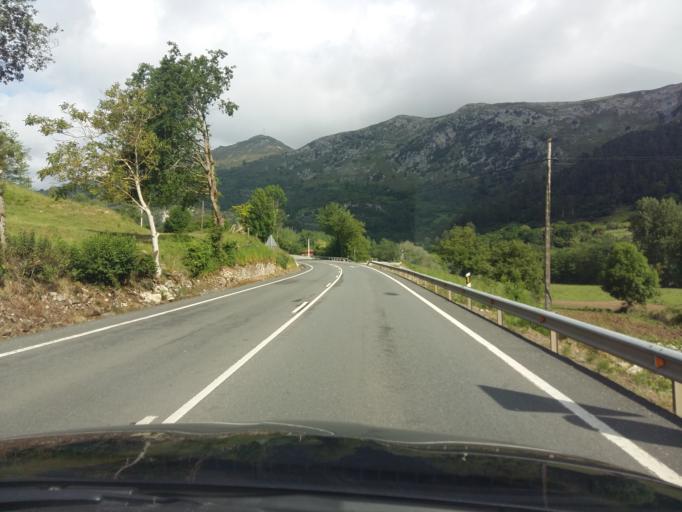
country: ES
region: Cantabria
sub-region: Provincia de Cantabria
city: Tresviso
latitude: 43.3271
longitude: -4.5722
